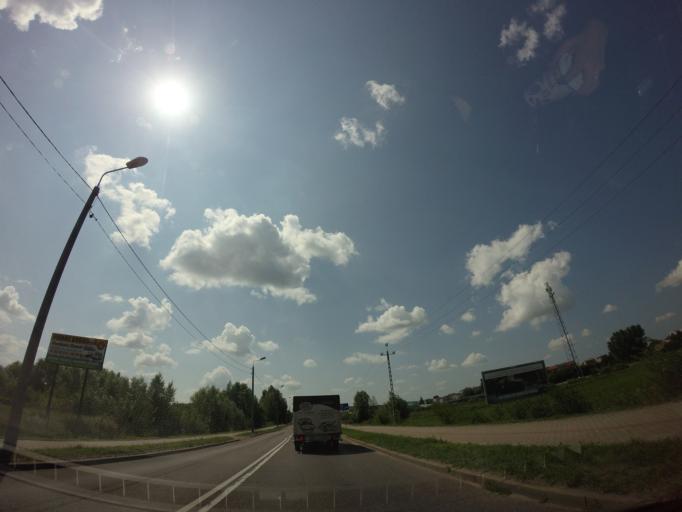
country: PL
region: Podlasie
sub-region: Powiat grajewski
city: Grajewo
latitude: 53.6499
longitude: 22.4673
